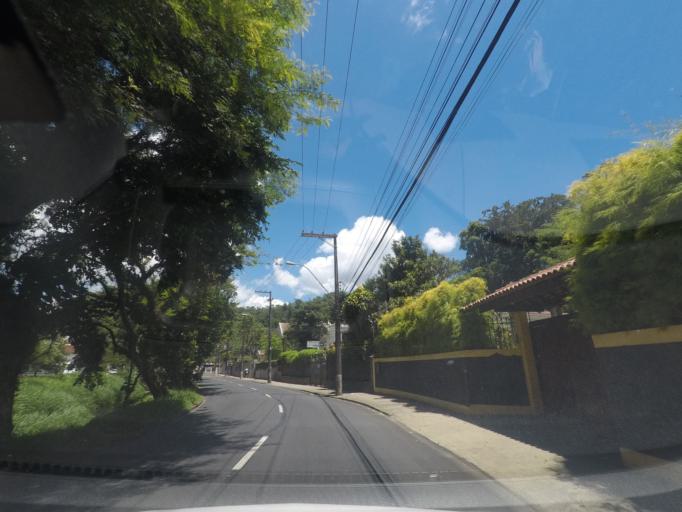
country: BR
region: Rio de Janeiro
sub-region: Petropolis
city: Petropolis
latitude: -22.5144
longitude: -43.1716
